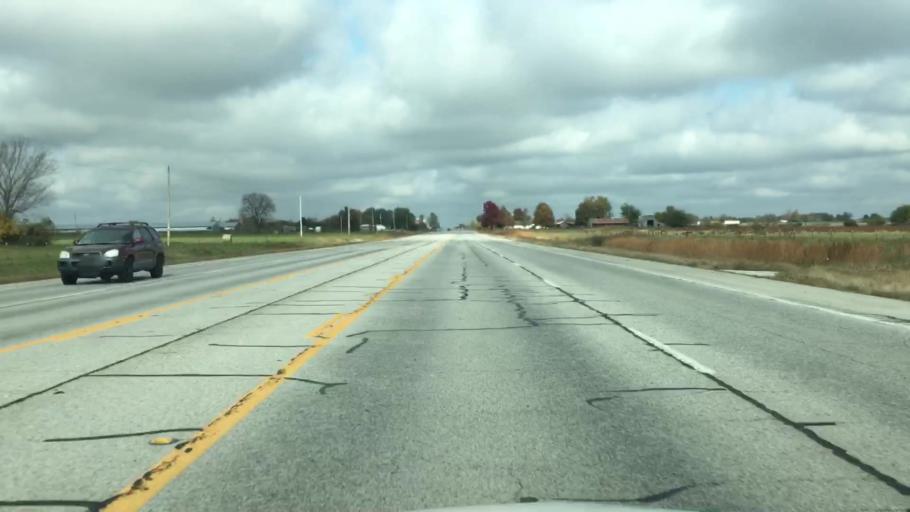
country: US
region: Arkansas
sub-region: Benton County
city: Siloam Springs
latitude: 36.2139
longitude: -94.4955
